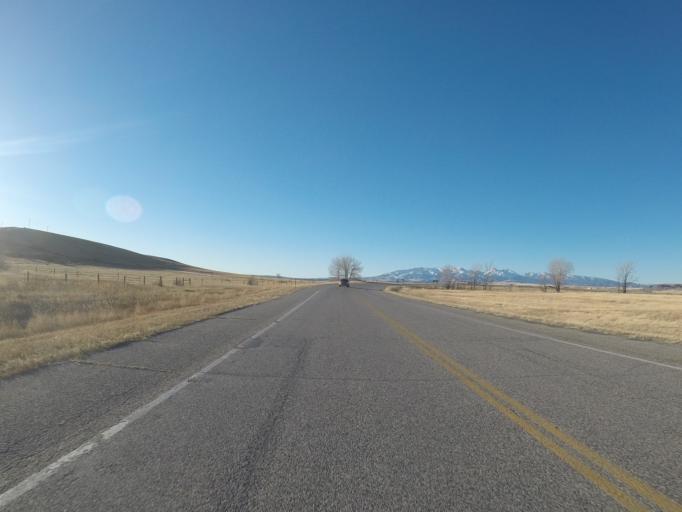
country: US
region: Montana
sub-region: Sweet Grass County
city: Big Timber
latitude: 45.8298
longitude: -109.9045
